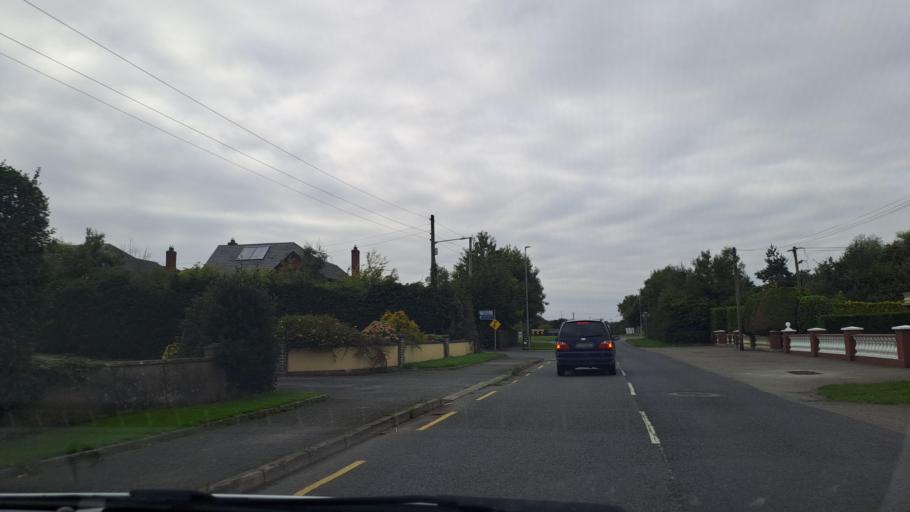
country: IE
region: Ulster
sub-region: County Monaghan
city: Carrickmacross
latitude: 53.9867
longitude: -6.7222
